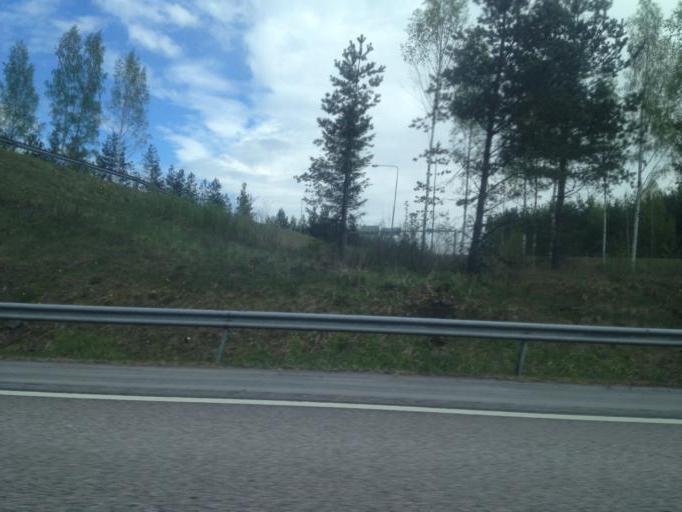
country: FI
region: Uusimaa
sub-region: Helsinki
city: Hyvinge
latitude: 60.6602
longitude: 24.7941
